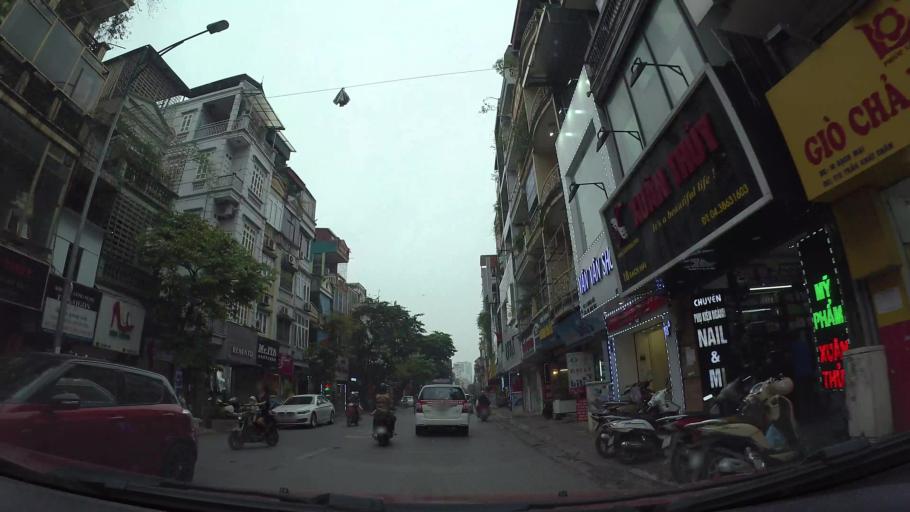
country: VN
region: Ha Noi
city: Hai BaTrung
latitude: 21.0082
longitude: 105.8514
